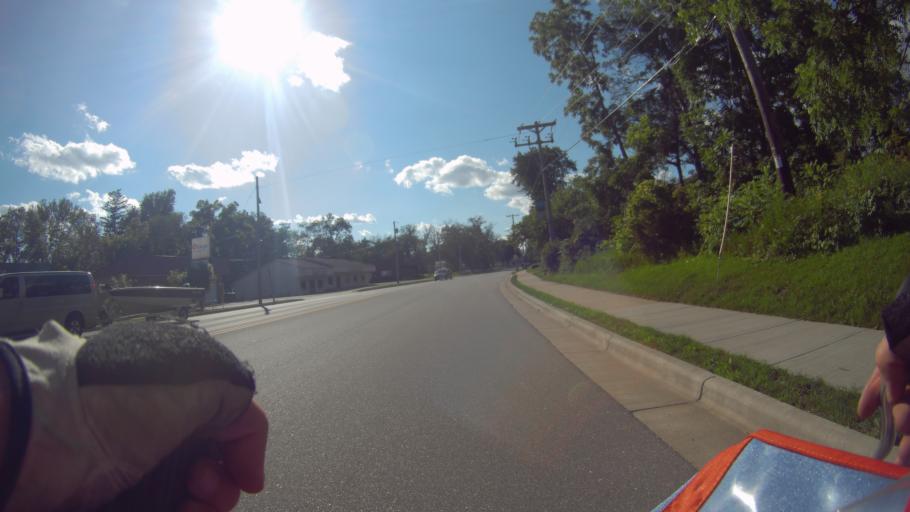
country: US
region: Wisconsin
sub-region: Dane County
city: Oregon
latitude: 42.9183
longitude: -89.3739
